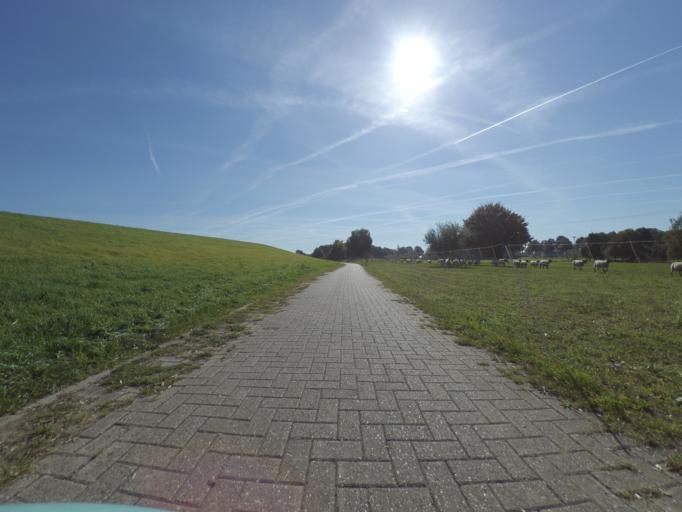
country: NL
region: Gelderland
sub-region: Gemeente Zevenaar
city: Zevenaar
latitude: 51.8552
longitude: 6.0743
